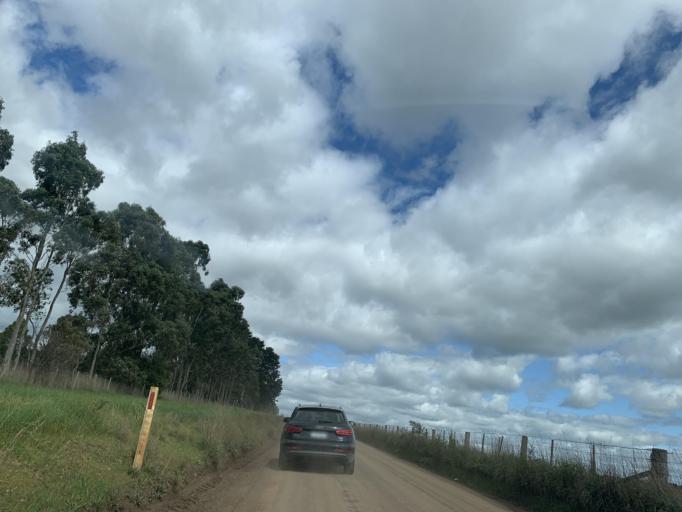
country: AU
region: Victoria
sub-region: Whittlesea
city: Whittlesea
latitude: -37.2828
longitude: 144.9299
